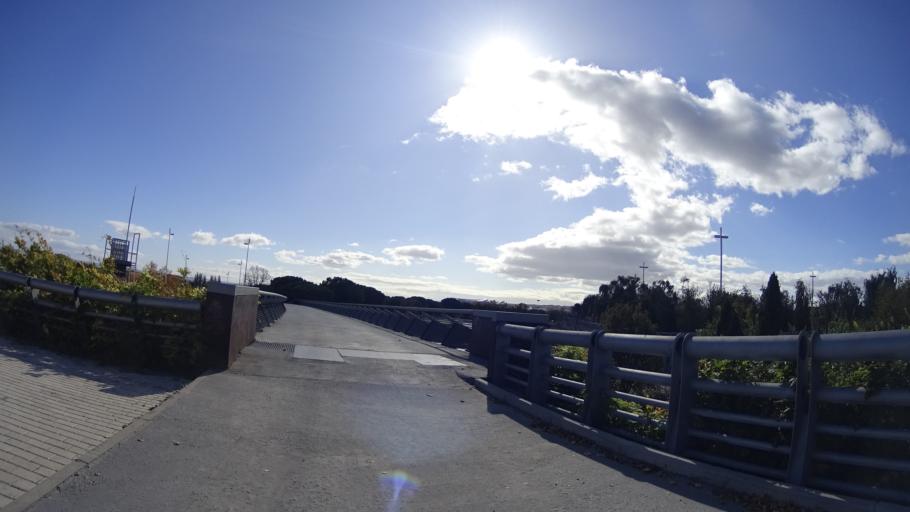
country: ES
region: Madrid
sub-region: Provincia de Madrid
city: San Blas
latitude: 40.4591
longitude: -3.6089
